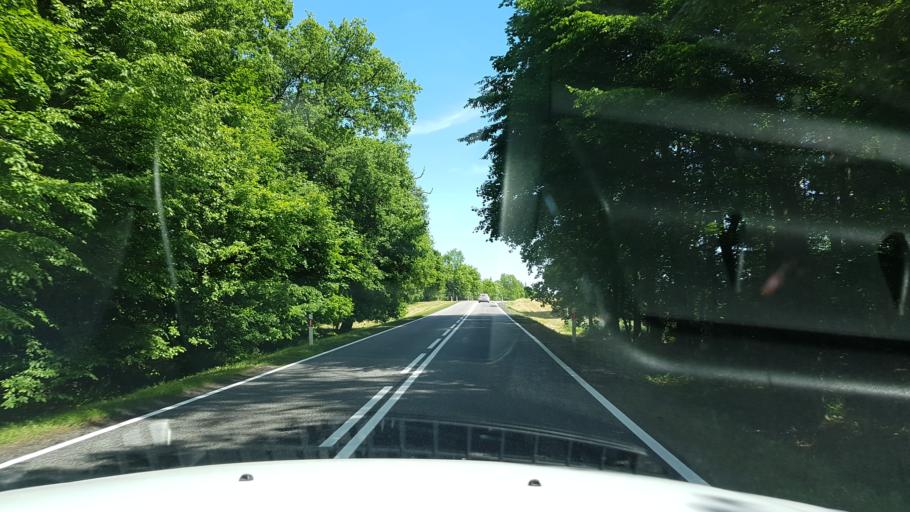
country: PL
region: West Pomeranian Voivodeship
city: Trzcinsko Zdroj
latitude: 52.9607
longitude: 14.5203
